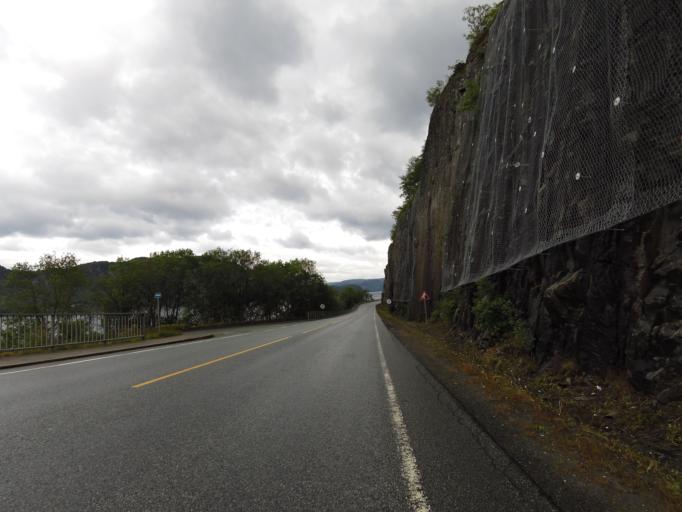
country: NO
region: Vest-Agder
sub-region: Farsund
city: Farsund
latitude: 58.0969
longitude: 6.8148
